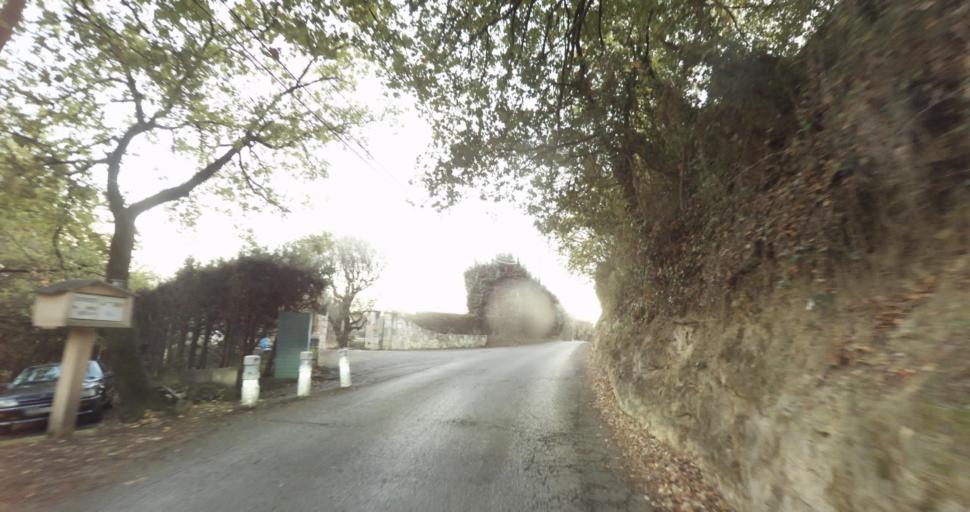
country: FR
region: Provence-Alpes-Cote d'Azur
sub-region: Departement des Alpes-Maritimes
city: Saint-Jeannet
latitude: 43.7347
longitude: 7.1293
